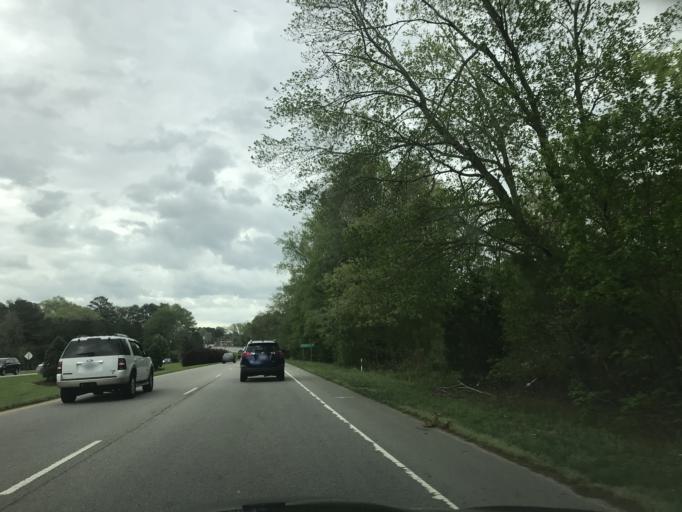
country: US
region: North Carolina
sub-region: Wake County
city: Knightdale
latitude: 35.7960
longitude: -78.5268
